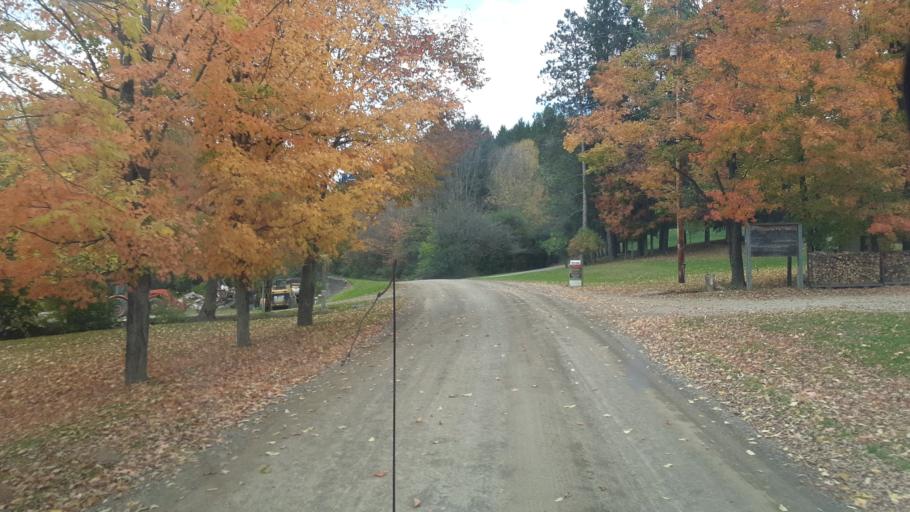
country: US
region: New York
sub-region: Allegany County
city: Alfred
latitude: 42.3679
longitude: -77.8428
